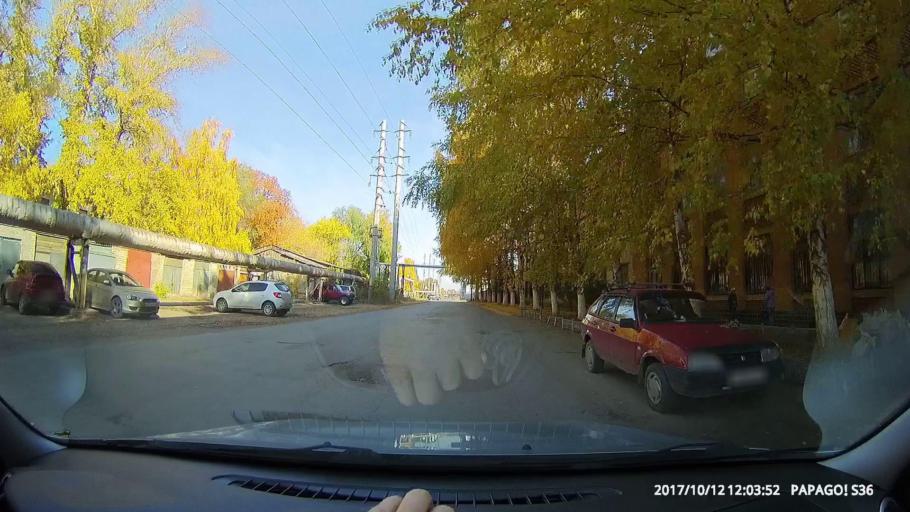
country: RU
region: Samara
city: Chapayevsk
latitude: 52.9768
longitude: 49.7166
